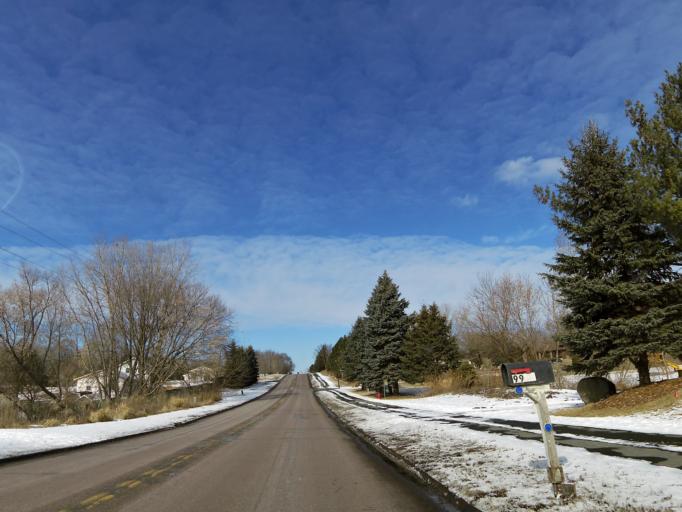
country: US
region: Minnesota
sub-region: Hennepin County
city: Eden Prairie
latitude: 44.8239
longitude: -93.4291
